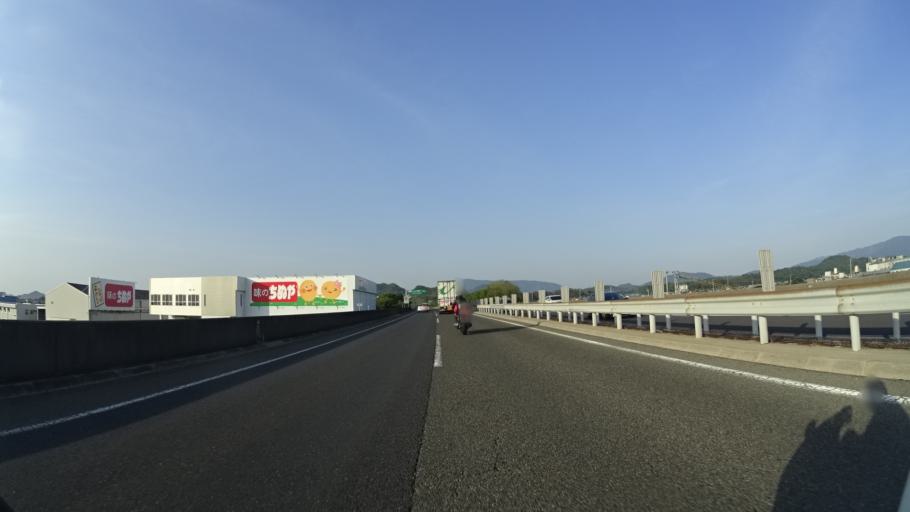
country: JP
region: Kagawa
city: Kan'onjicho
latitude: 34.1319
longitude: 133.7051
